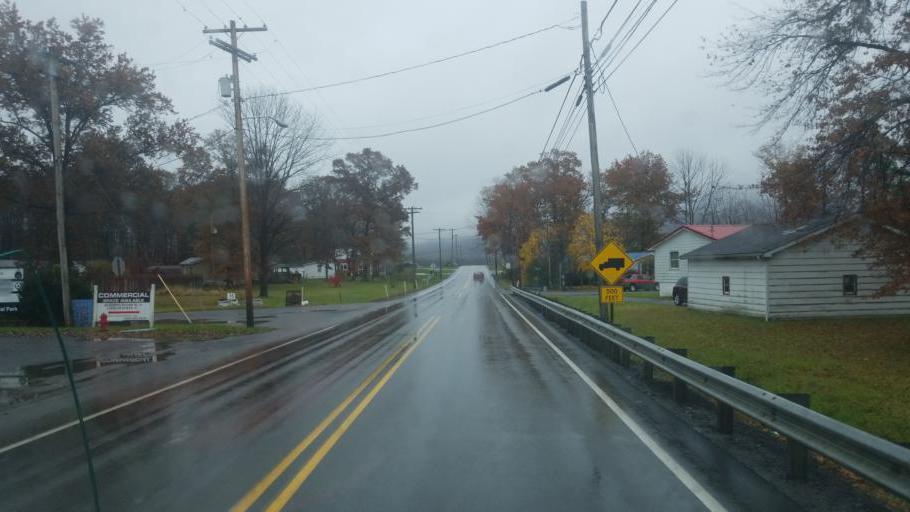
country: US
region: Pennsylvania
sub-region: Clinton County
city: Mill Hall
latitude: 41.0756
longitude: -77.5741
